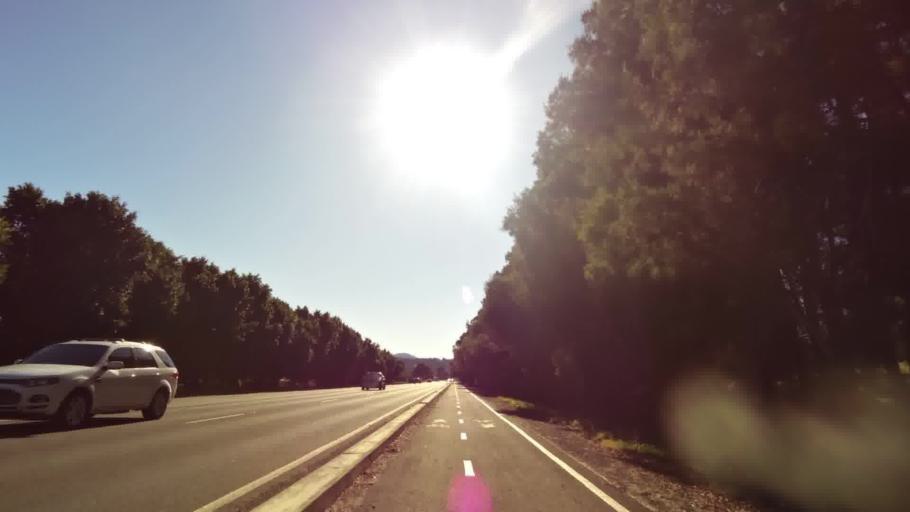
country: AU
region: New South Wales
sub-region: Wollongong
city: Koonawarra
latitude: -34.4863
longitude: 150.7997
